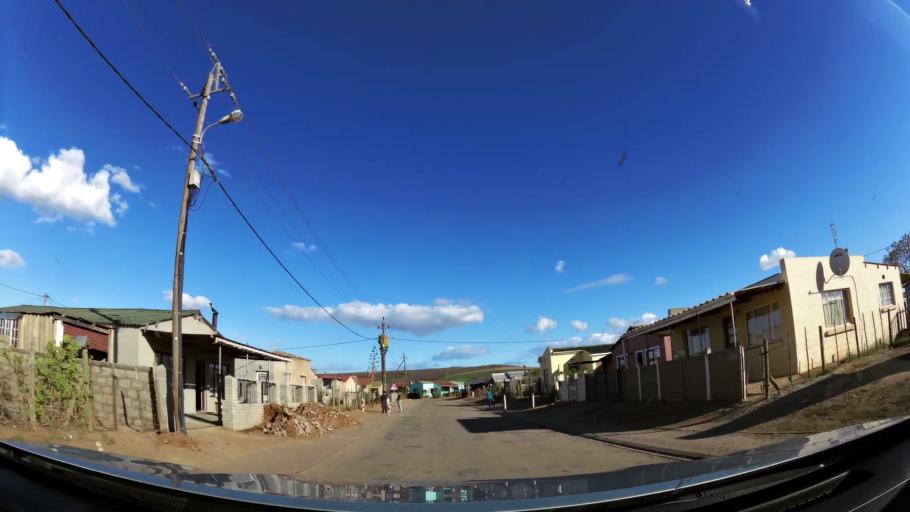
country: ZA
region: Western Cape
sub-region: Eden District Municipality
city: Riversdale
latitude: -34.1066
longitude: 20.9620
